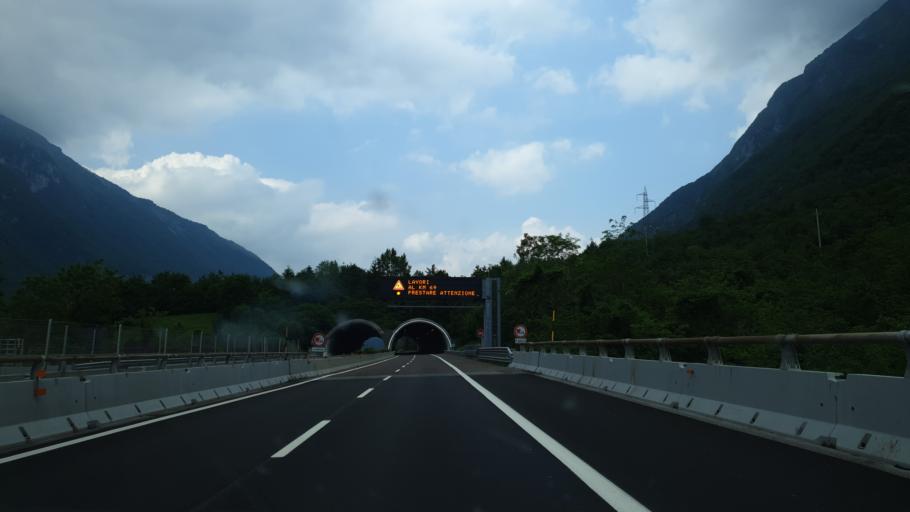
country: IT
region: Veneto
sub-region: Provincia di Treviso
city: Fregona
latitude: 46.0404
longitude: 12.3118
